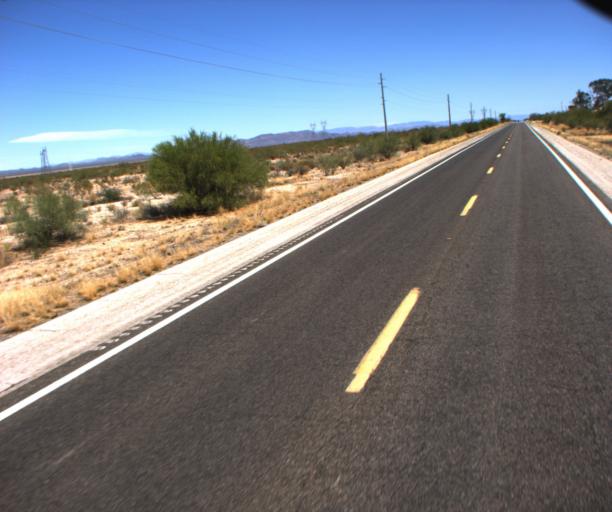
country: US
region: Arizona
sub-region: La Paz County
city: Salome
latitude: 33.9012
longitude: -113.3035
